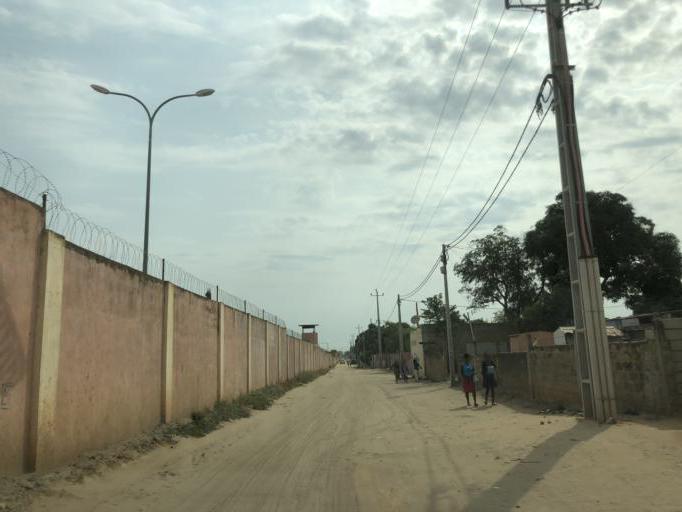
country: AO
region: Luanda
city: Luanda
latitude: -8.8966
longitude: 13.3542
